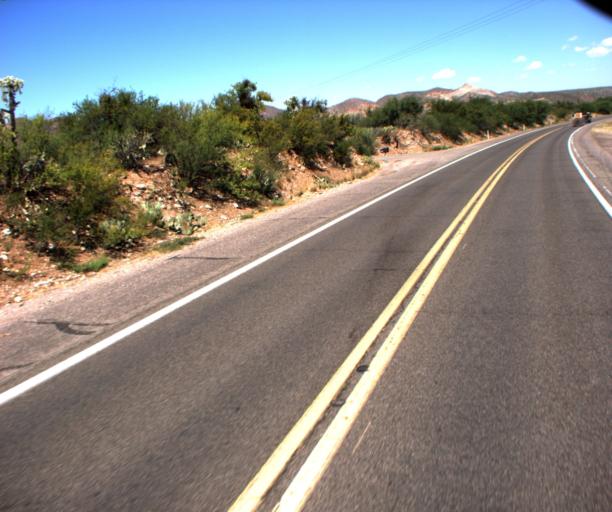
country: US
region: Arizona
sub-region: Pinal County
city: Mammoth
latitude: 32.8329
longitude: -110.7056
